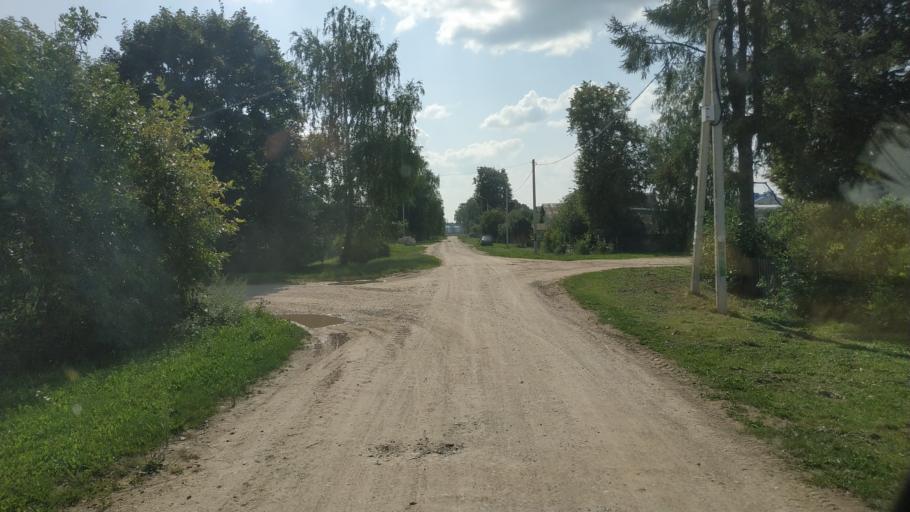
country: BY
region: Mogilev
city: Buynichy
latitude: 53.9653
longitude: 30.1928
